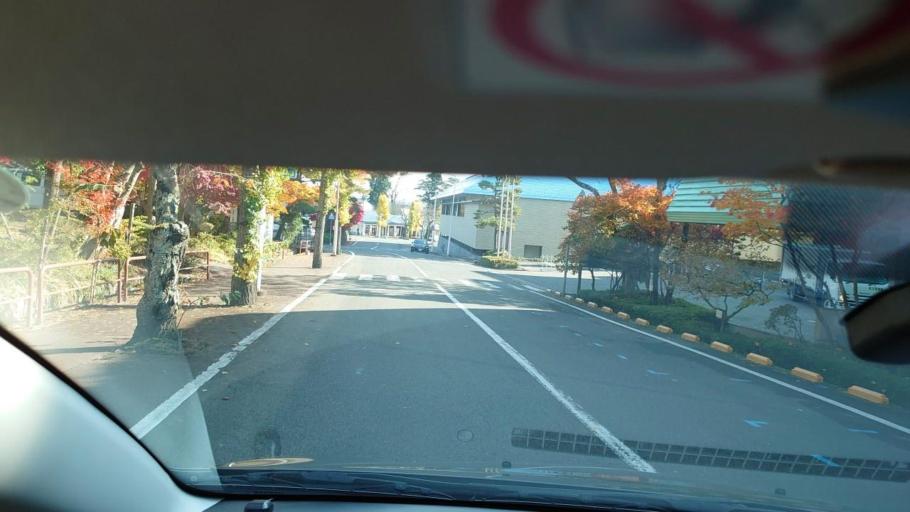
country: JP
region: Iwate
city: Hanamaki
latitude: 39.4525
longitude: 141.0691
